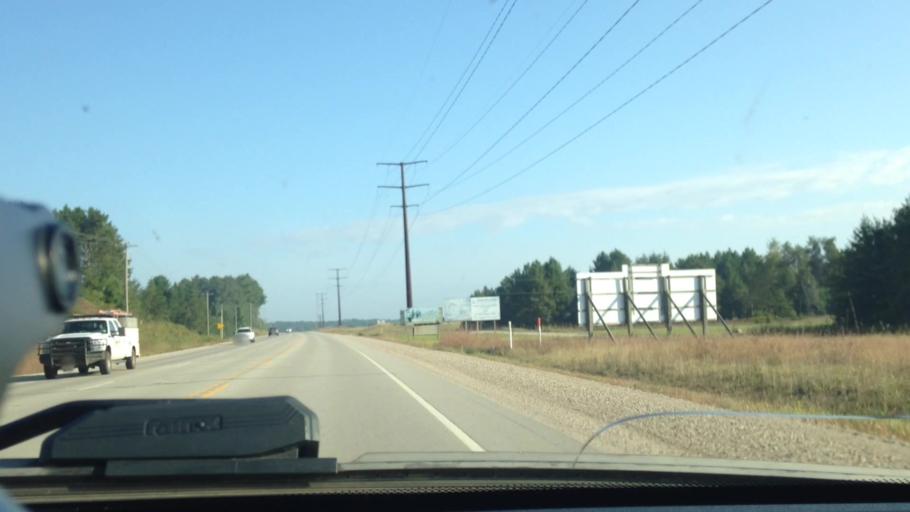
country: US
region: Wisconsin
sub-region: Marinette County
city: Peshtigo
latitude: 45.1971
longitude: -87.9944
